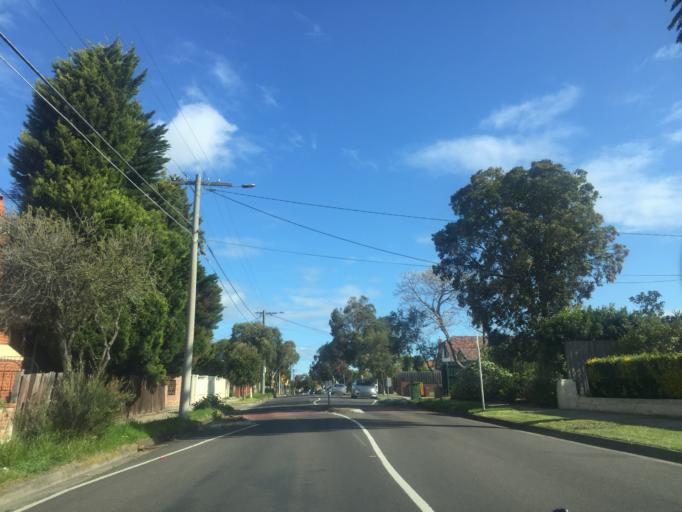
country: AU
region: Victoria
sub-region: Darebin
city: Reservoir
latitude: -37.7290
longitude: 145.0141
